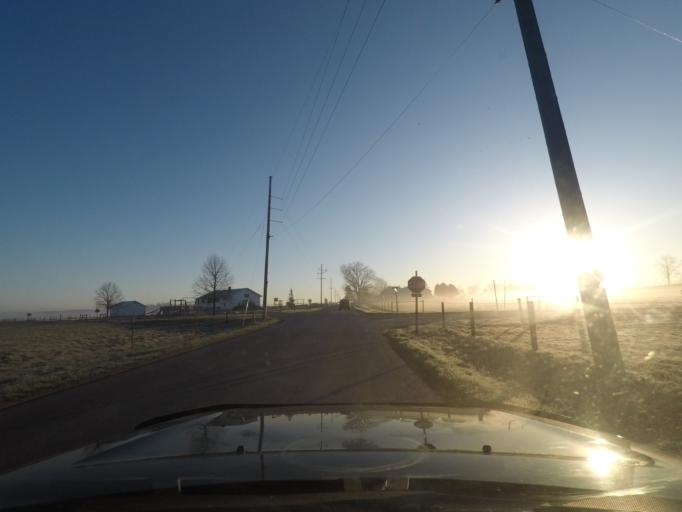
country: US
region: Indiana
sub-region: Marshall County
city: Bremen
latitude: 41.4618
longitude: -86.0790
